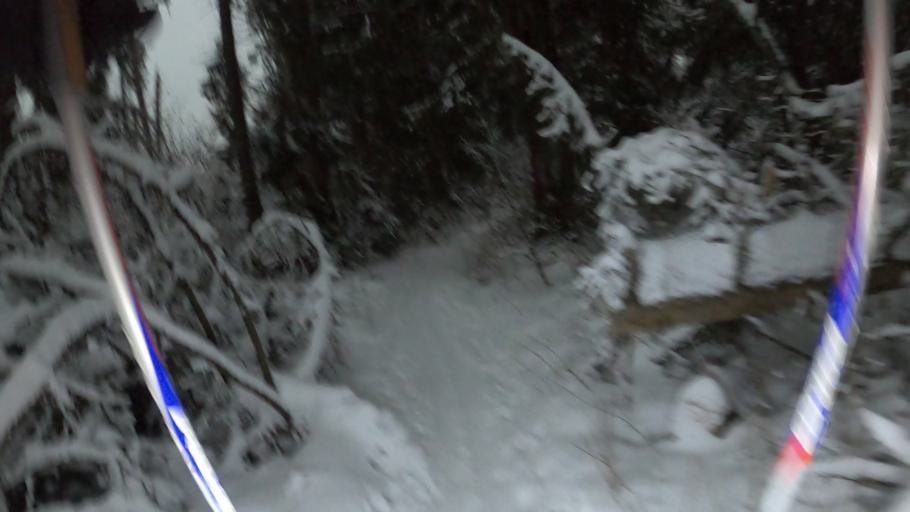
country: RU
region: Moskovskaya
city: Nakhabino
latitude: 55.8936
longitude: 37.2088
